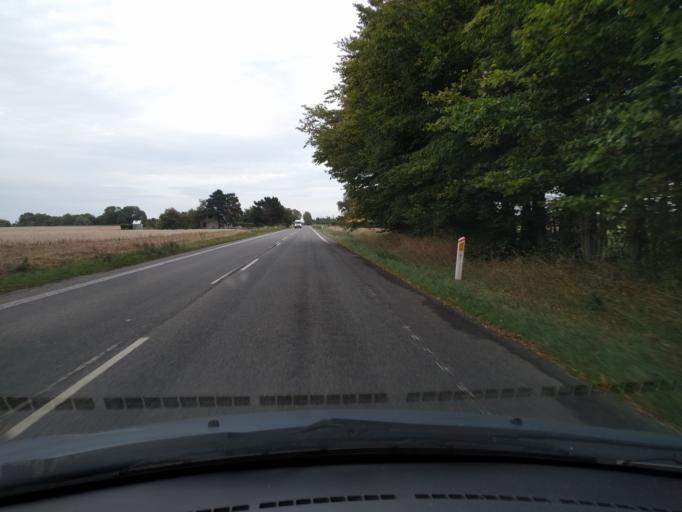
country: DK
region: Zealand
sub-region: Guldborgsund Kommune
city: Stubbekobing
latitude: 54.8937
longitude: 11.9874
